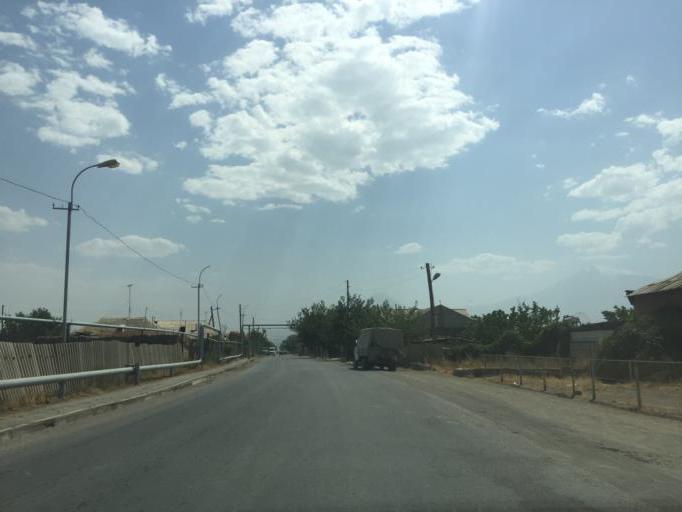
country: AM
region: Ararat
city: Shahumyan
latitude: 39.8998
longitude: 44.5987
